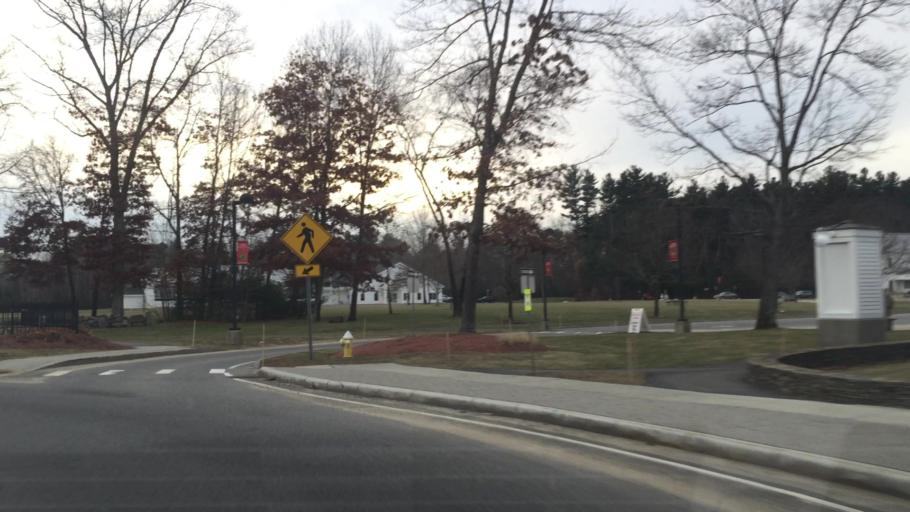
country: US
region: New Hampshire
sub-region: Hillsborough County
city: Pelham
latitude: 42.7322
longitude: -71.3244
